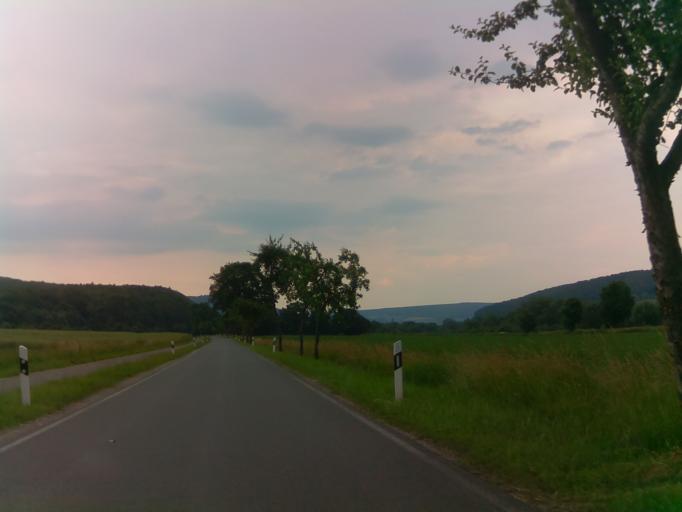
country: DE
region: Lower Saxony
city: Polle
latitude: 51.8941
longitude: 9.4111
